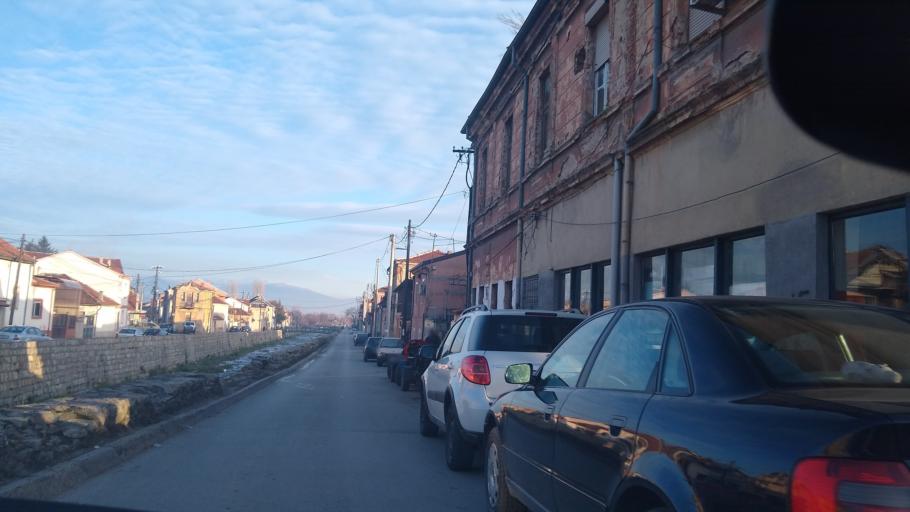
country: MK
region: Bitola
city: Bitola
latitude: 41.0312
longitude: 21.3416
